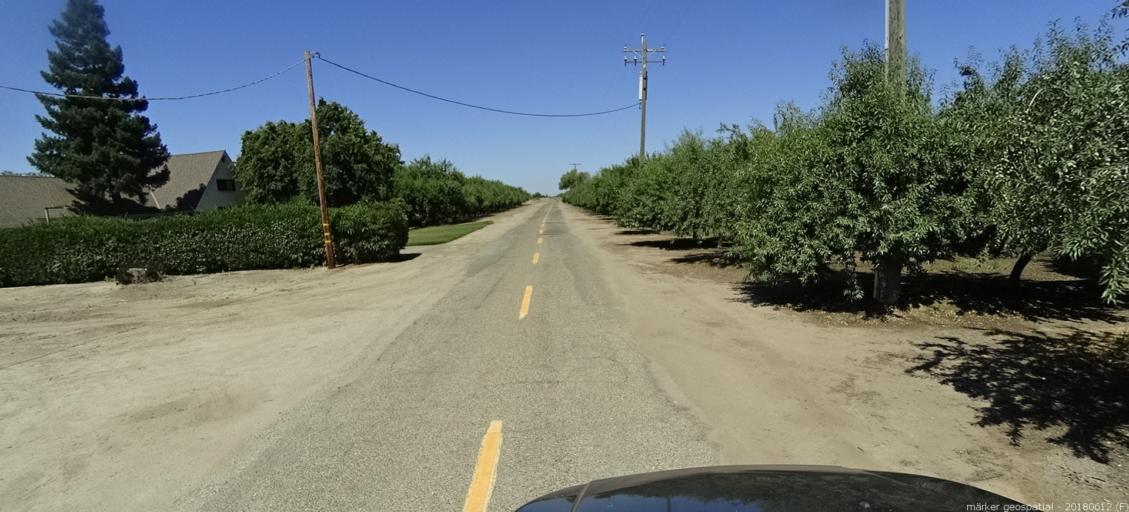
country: US
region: California
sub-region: Madera County
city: Chowchilla
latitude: 37.0255
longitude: -120.3060
